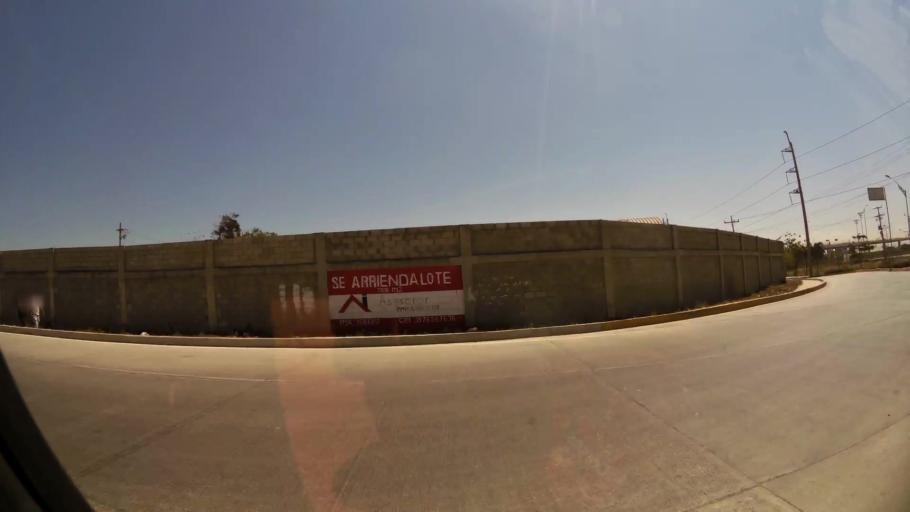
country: CO
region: Atlantico
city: Barranquilla
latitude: 10.9870
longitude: -74.7700
